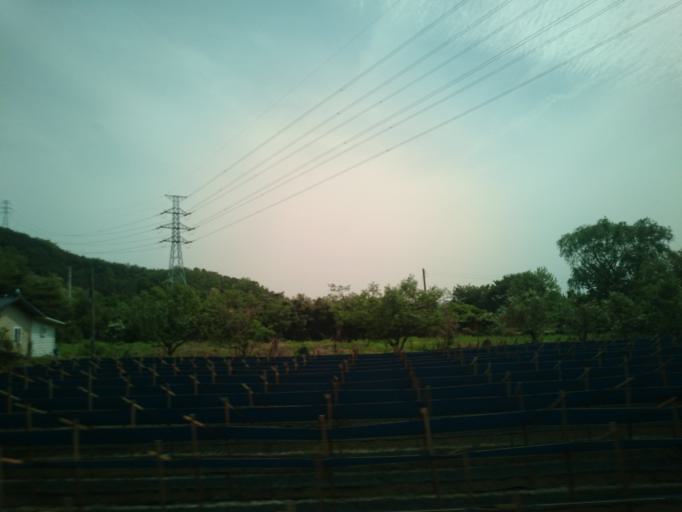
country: KR
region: Jeollabuk-do
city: Wanju
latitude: 35.9001
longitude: 127.1954
